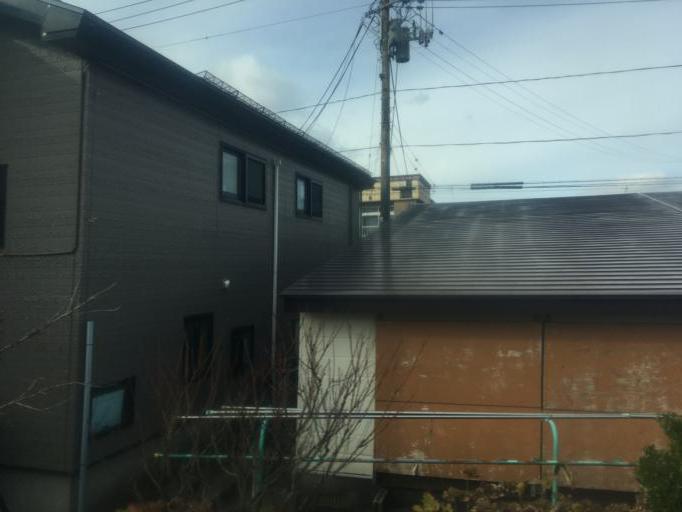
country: JP
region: Akita
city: Tenno
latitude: 39.8683
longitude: 140.0619
